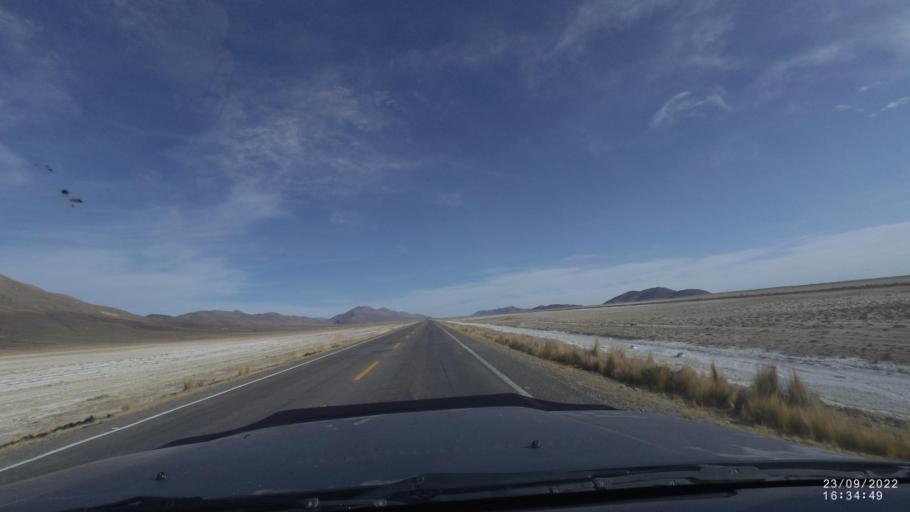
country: BO
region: Oruro
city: Machacamarca
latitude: -18.1949
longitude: -67.0132
